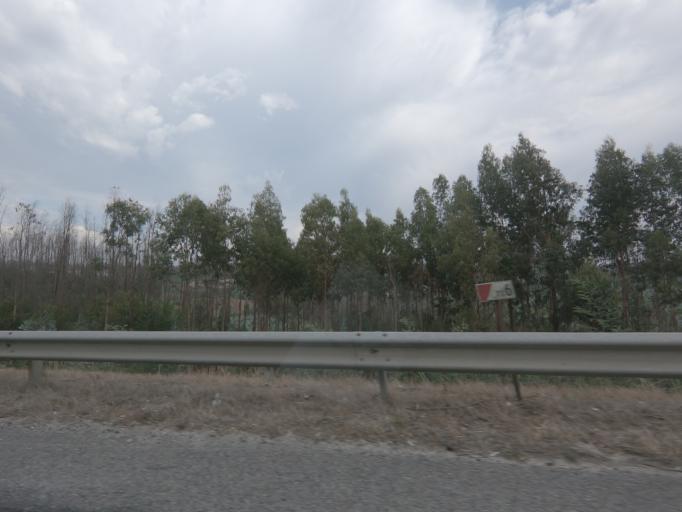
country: PT
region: Viseu
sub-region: Santa Comba Dao
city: Santa Comba Dao
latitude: 40.3510
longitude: -8.1586
